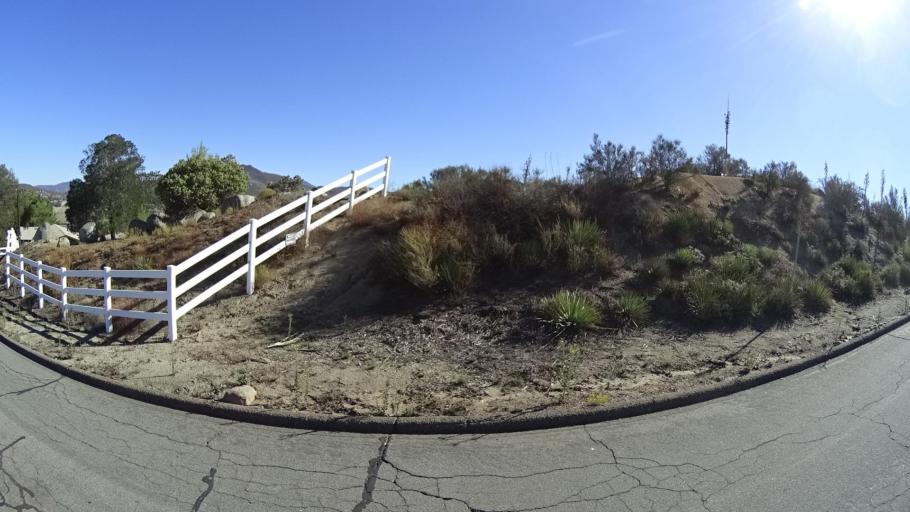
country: US
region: California
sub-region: San Diego County
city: Alpine
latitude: 32.8354
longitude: -116.7003
